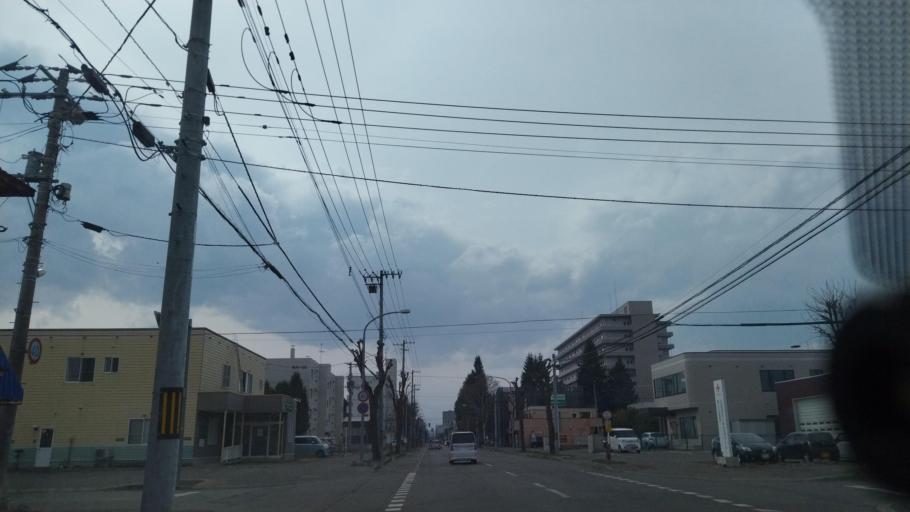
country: JP
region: Hokkaido
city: Obihiro
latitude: 42.9224
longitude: 143.2168
